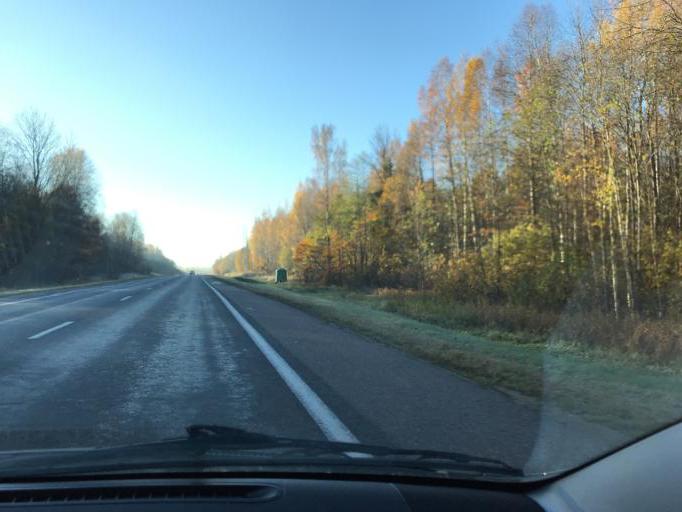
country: BY
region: Vitebsk
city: Vitebsk
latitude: 54.9320
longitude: 30.3704
